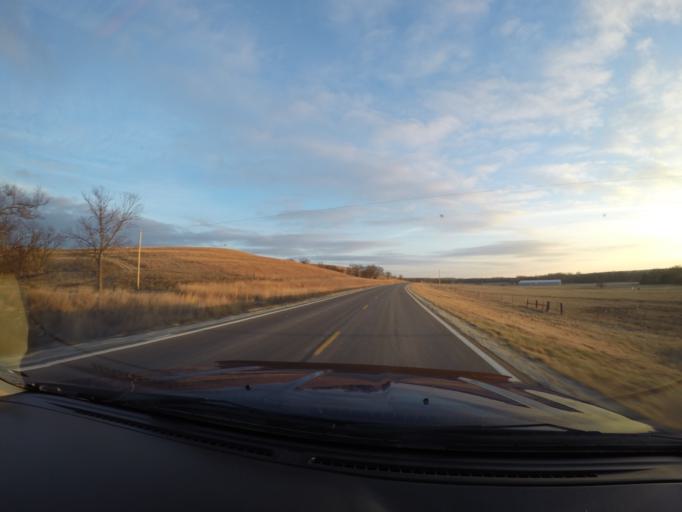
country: US
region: Kansas
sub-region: Chase County
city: Cottonwood Falls
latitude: 38.4590
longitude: -96.5516
